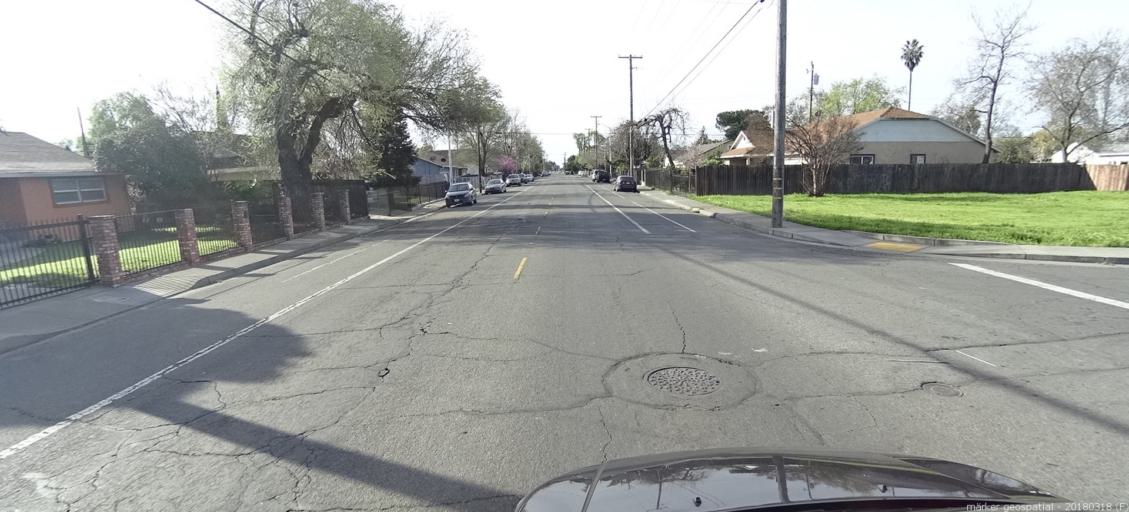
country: US
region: California
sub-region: Sacramento County
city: Parkway
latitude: 38.5310
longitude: -121.4647
